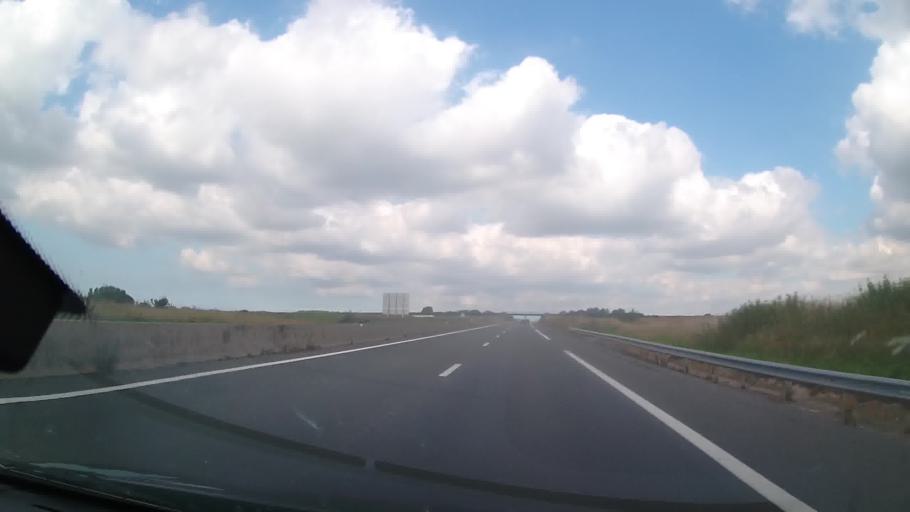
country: FR
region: Picardie
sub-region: Departement de la Somme
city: Rue
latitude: 50.3041
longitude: 1.7253
